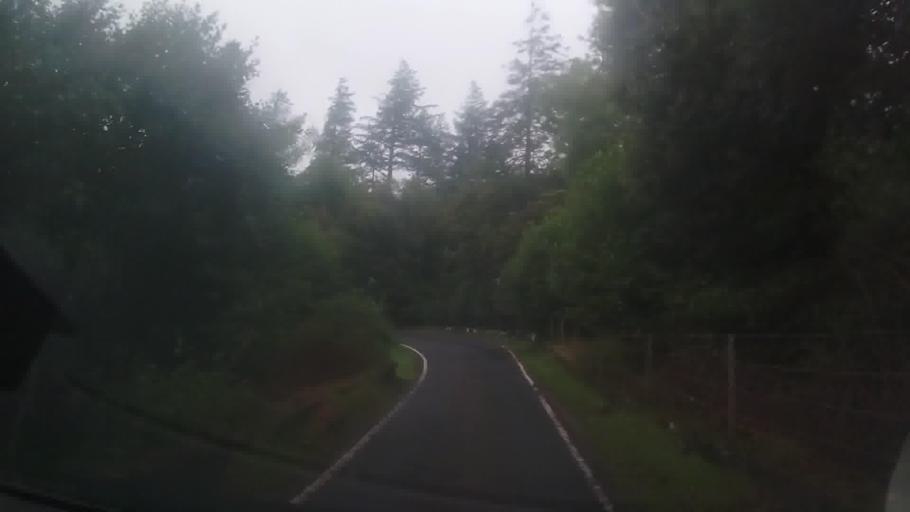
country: GB
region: Scotland
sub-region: Argyll and Bute
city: Isle Of Mull
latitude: 56.6803
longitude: -5.9037
